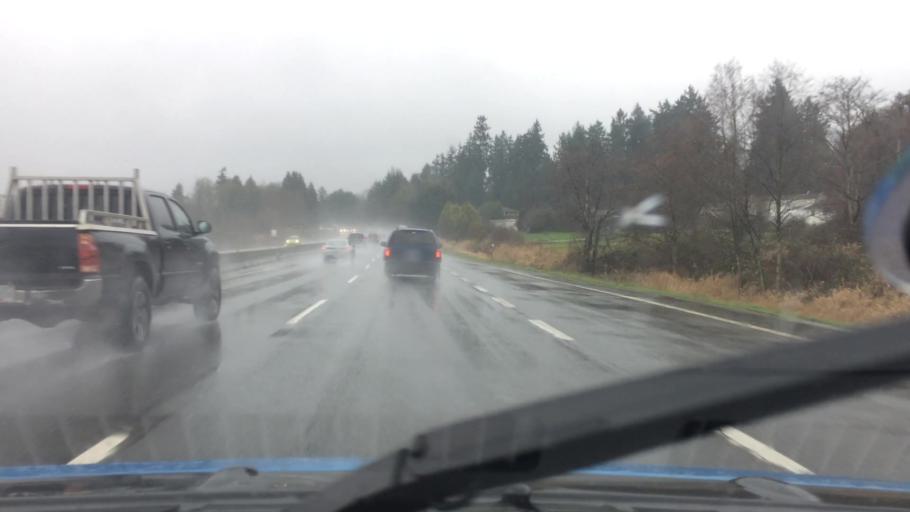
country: CA
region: British Columbia
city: North Saanich
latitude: 48.5712
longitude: -123.3986
